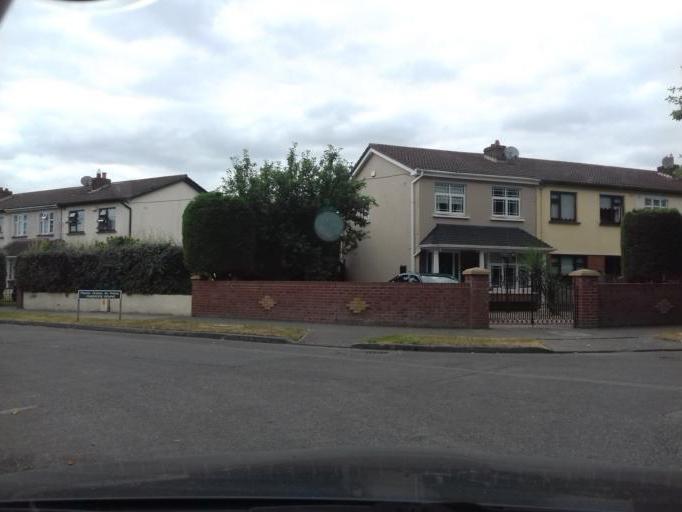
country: IE
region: Leinster
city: Hartstown
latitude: 53.3970
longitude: -6.4112
